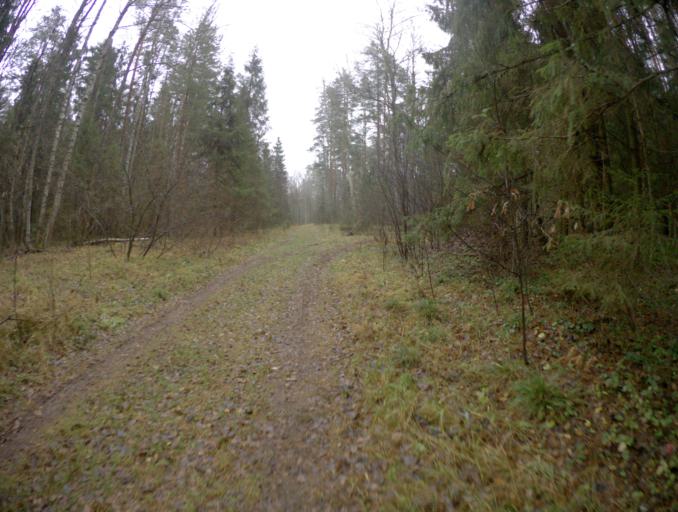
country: RU
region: Vladimir
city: Golovino
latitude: 56.0107
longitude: 40.4847
